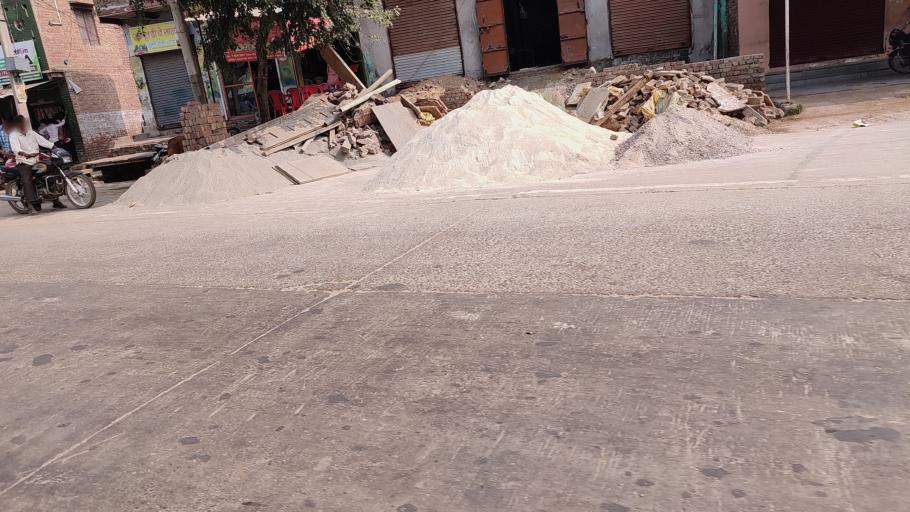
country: IN
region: Uttar Pradesh
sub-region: Mathura
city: Barsana
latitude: 27.6552
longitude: 77.3820
